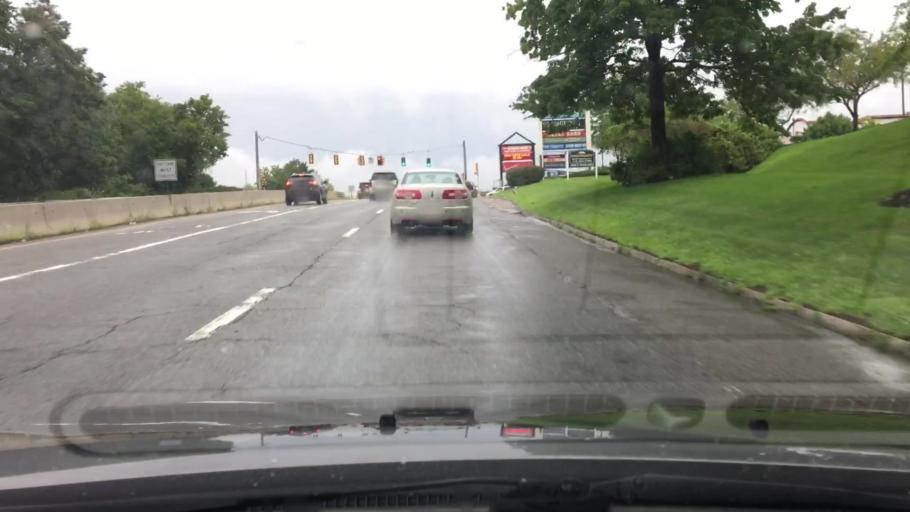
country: US
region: Rhode Island
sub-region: Providence County
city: Valley Falls
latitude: 41.9400
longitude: -71.3492
